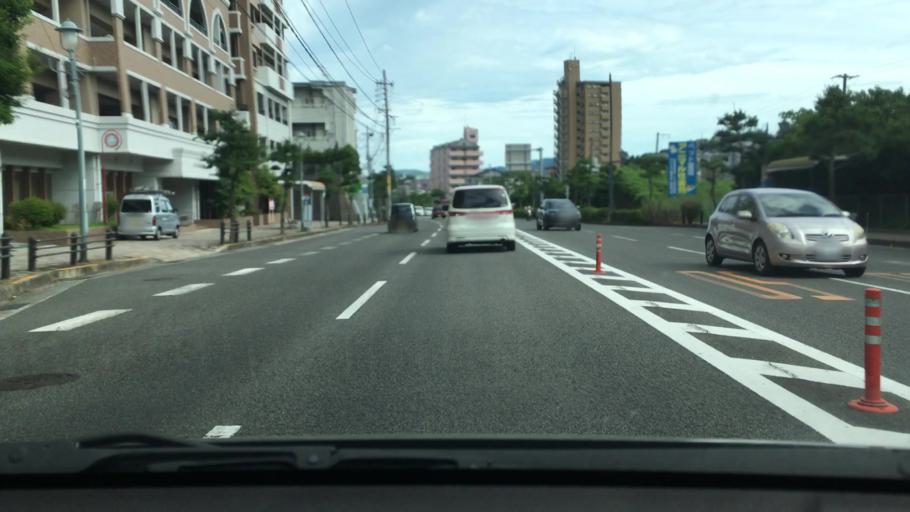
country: JP
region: Nagasaki
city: Obita
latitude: 32.7976
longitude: 129.8545
